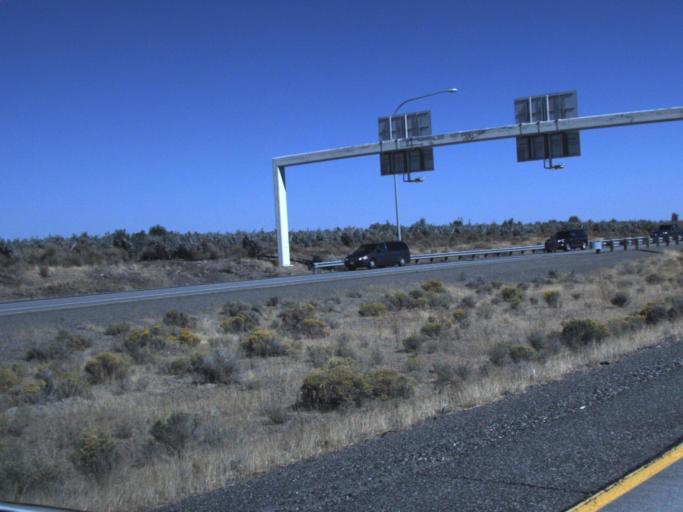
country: US
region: Washington
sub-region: Benton County
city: West Richland
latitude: 46.2446
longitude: -119.3558
